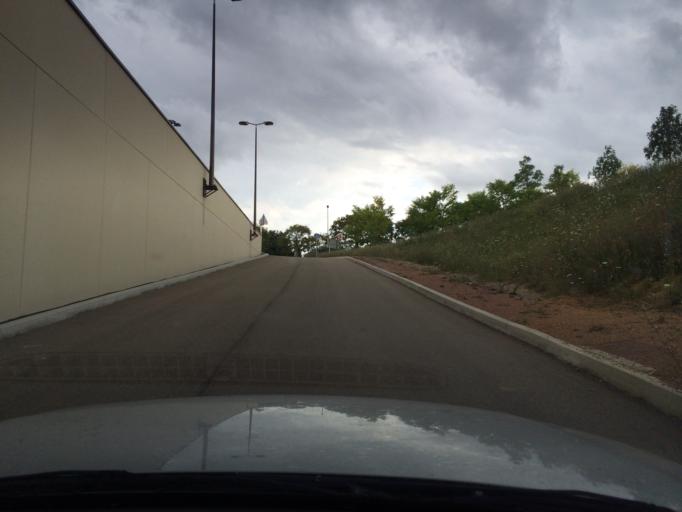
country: FR
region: Bourgogne
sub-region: Departement de l'Yonne
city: Auxerre
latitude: 47.8159
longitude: 3.5704
